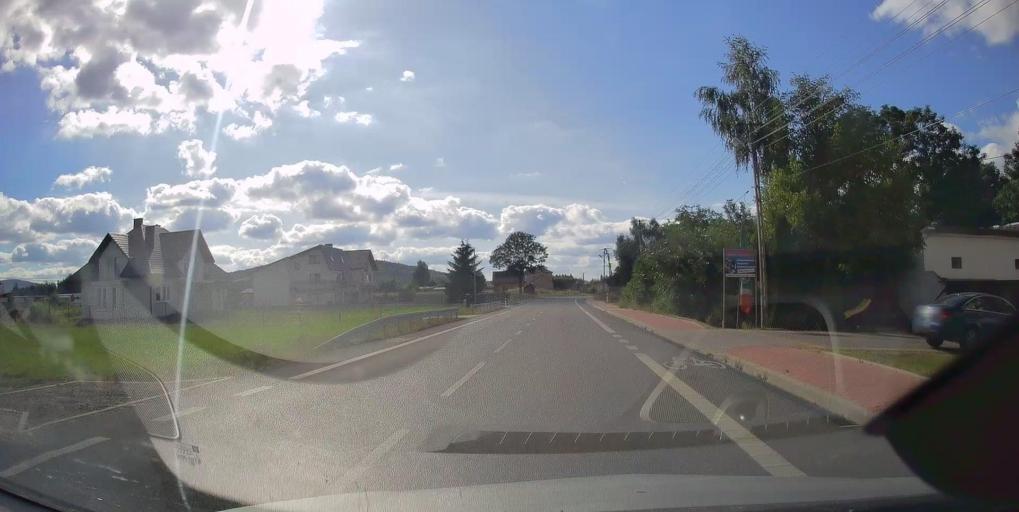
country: PL
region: Swietokrzyskie
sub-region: Powiat kielecki
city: Bodzentyn
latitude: 50.9317
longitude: 20.9737
